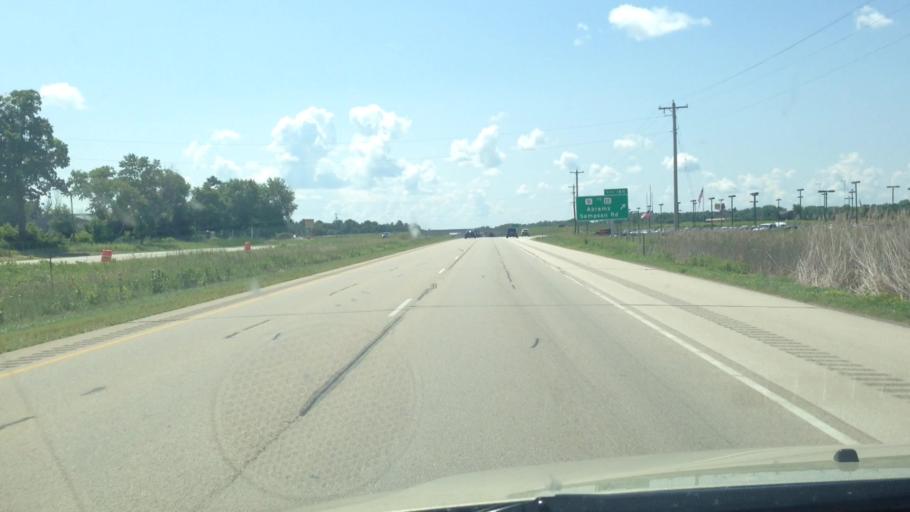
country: US
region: Wisconsin
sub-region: Oconto County
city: Oconto Falls
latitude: 44.7707
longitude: -88.0508
